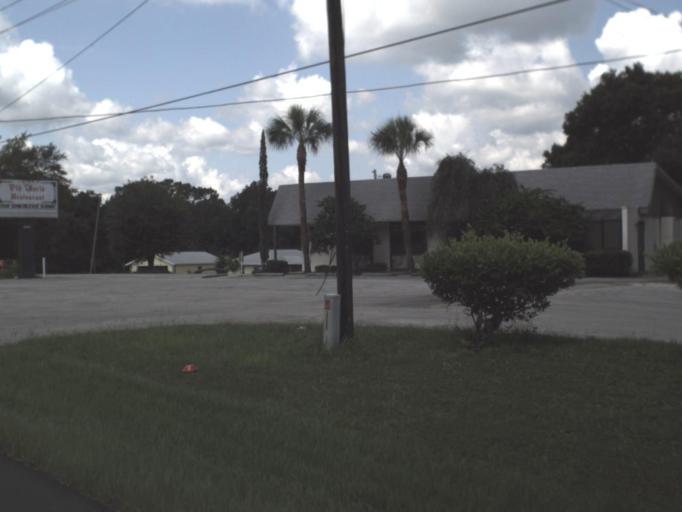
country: US
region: Florida
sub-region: Citrus County
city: Floral City
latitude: 28.7414
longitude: -82.3002
